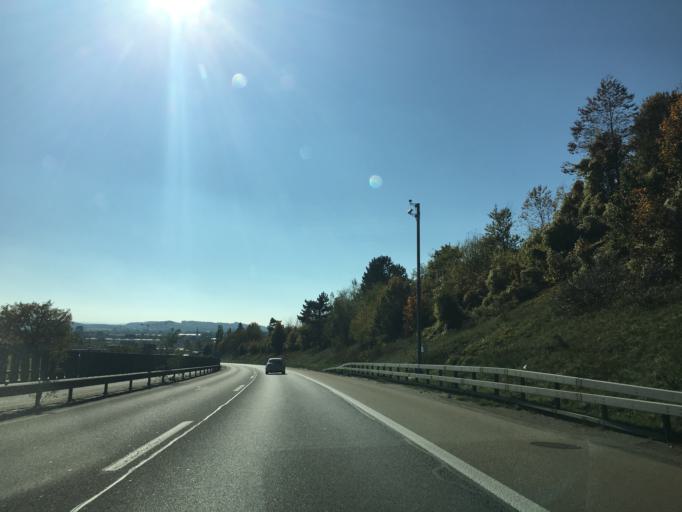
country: CH
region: Solothurn
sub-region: Bezirk Gaeu
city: Egerkingen
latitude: 47.3272
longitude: 7.8087
